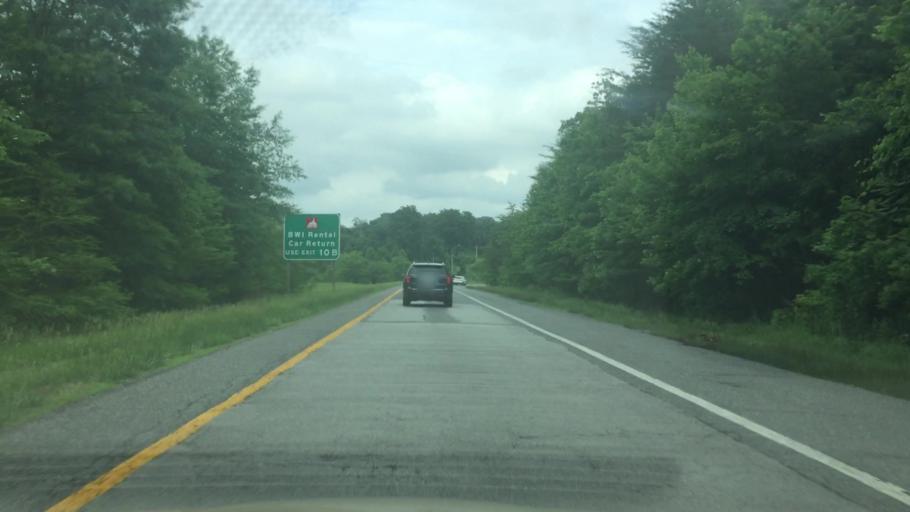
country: US
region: Maryland
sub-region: Howard County
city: Hanover
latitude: 39.1679
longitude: -76.7314
